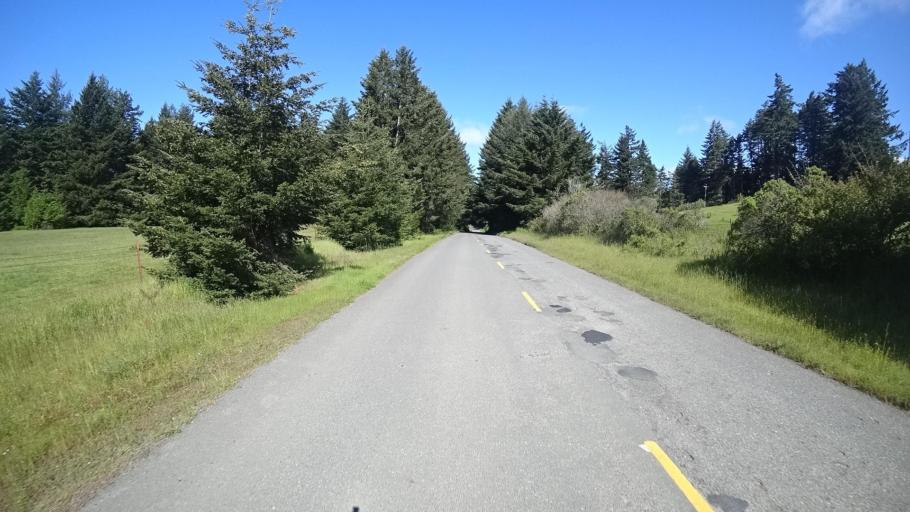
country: US
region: California
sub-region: Humboldt County
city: Ferndale
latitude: 40.3435
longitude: -124.3230
